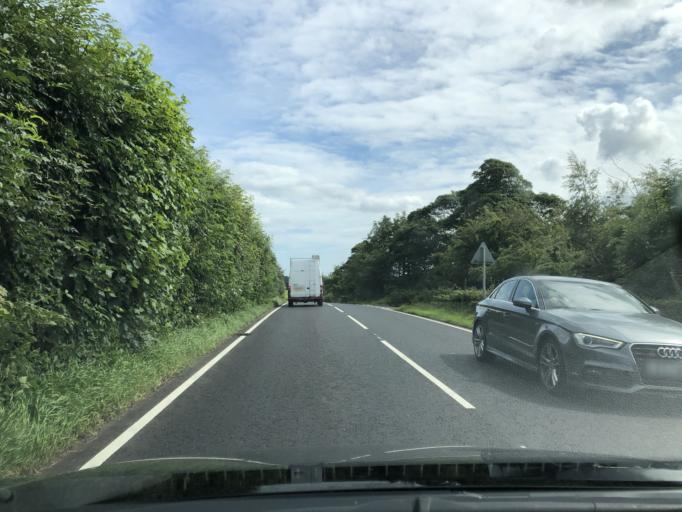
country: GB
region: Northern Ireland
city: Annahilt
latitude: 54.4439
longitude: -5.9457
